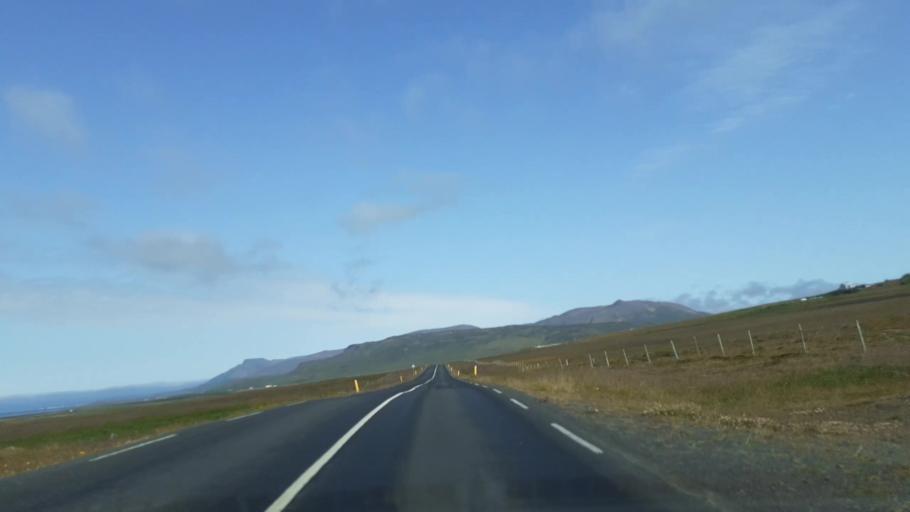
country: IS
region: Northwest
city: Saudarkrokur
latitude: 65.6978
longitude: -20.2384
